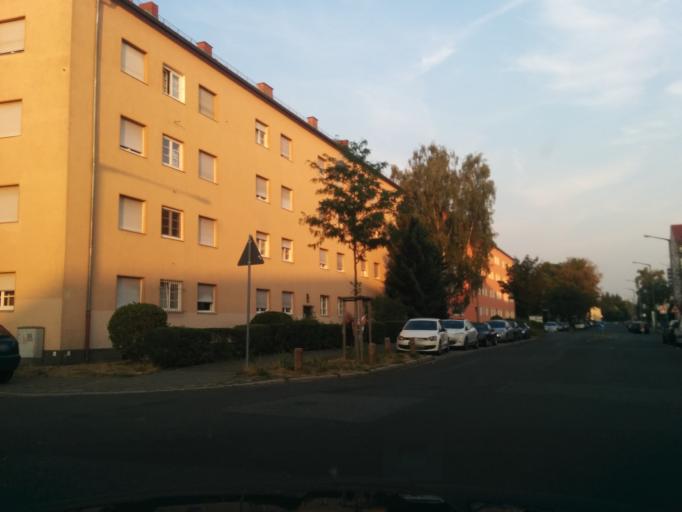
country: DE
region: Bavaria
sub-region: Regierungsbezirk Mittelfranken
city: Nuernberg
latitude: 49.4710
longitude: 11.1062
